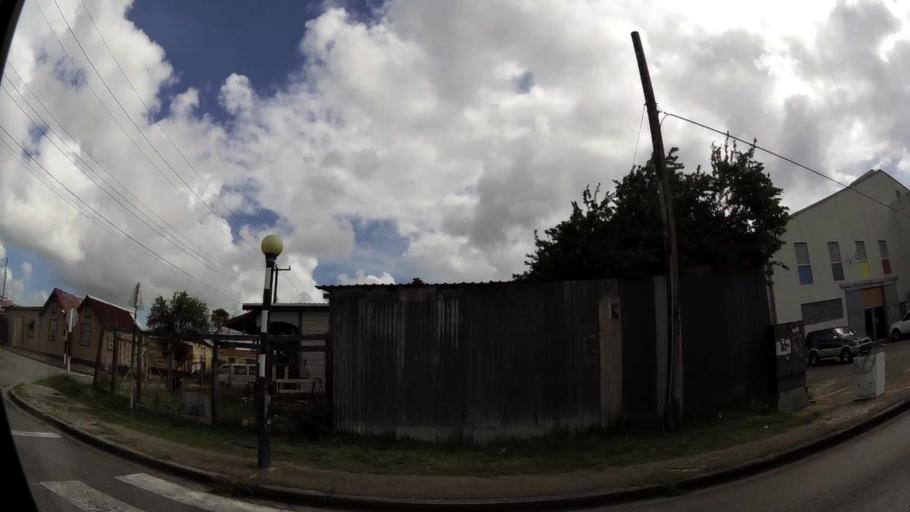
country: BB
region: Saint Michael
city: Bridgetown
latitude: 13.1108
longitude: -59.6167
